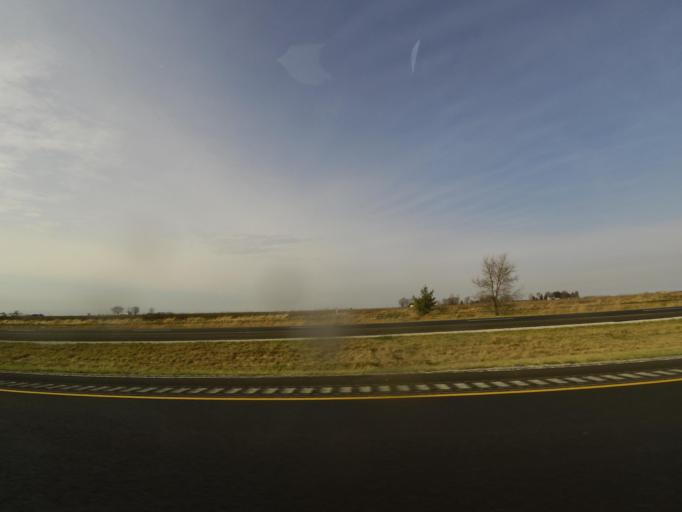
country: US
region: Illinois
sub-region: Macon County
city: Macon
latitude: 39.7354
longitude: -88.9910
